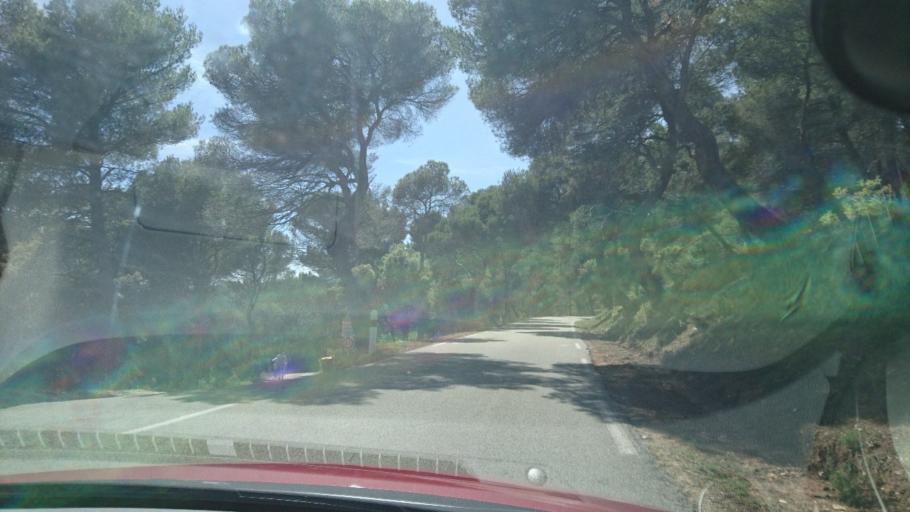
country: FR
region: Provence-Alpes-Cote d'Azur
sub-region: Departement du Vaucluse
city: Bedoin
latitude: 44.1410
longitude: 5.1551
